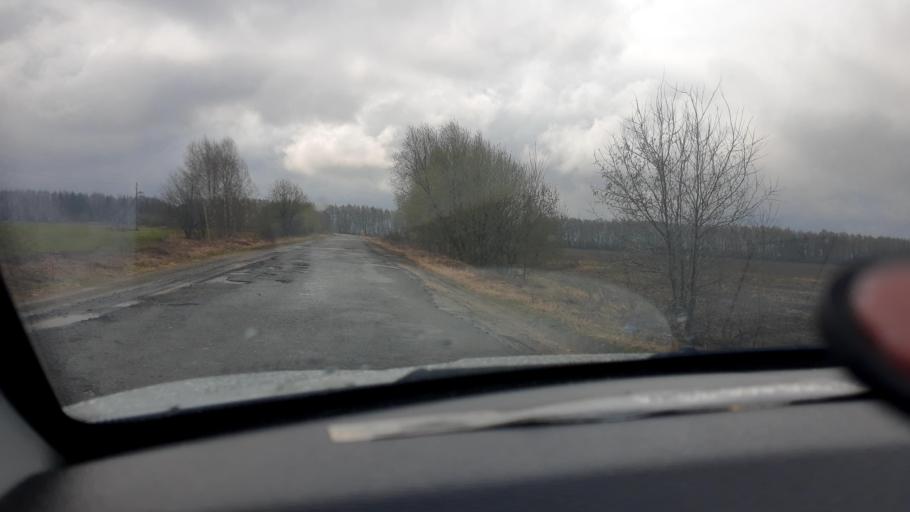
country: RU
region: Nizjnij Novgorod
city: Burevestnik
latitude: 56.1593
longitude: 43.6989
